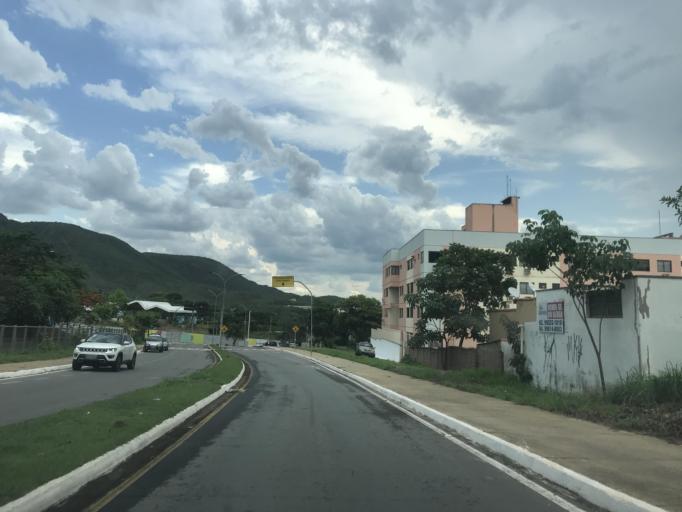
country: BR
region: Goias
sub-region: Caldas Novas
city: Caldas Novas
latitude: -17.7691
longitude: -48.7549
